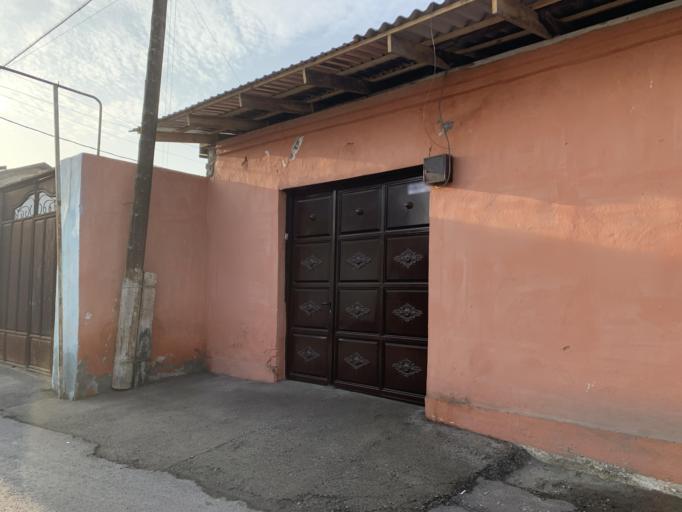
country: UZ
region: Fergana
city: Qo`qon
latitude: 40.5387
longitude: 70.9303
